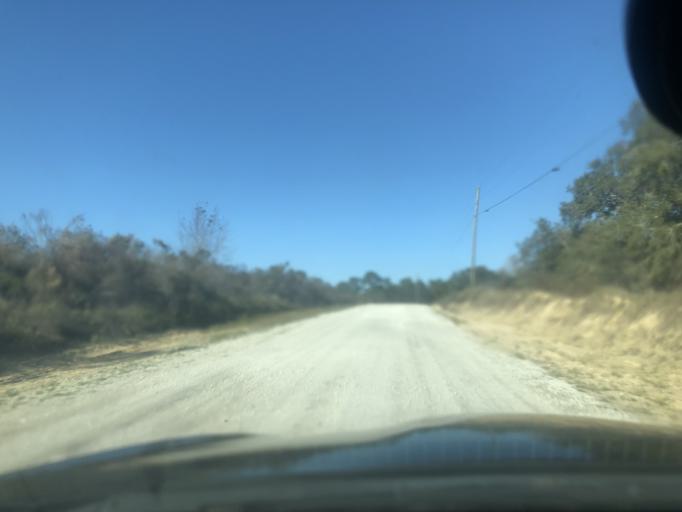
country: US
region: Florida
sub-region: Citrus County
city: Lecanto
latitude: 28.8245
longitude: -82.5181
